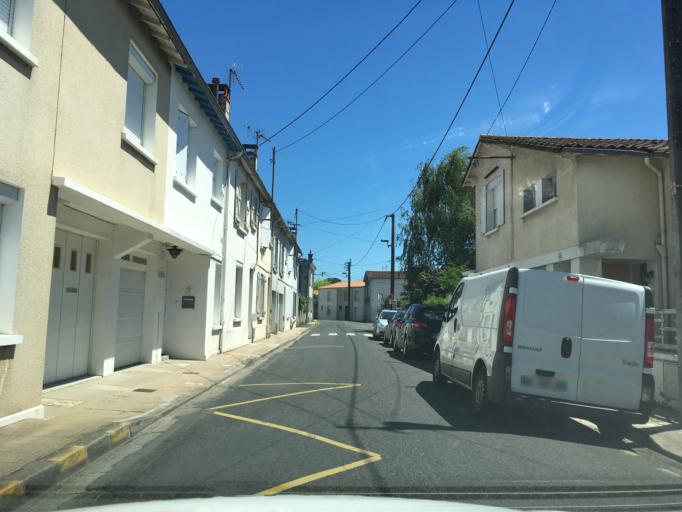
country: FR
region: Poitou-Charentes
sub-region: Departement des Deux-Sevres
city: Niort
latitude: 46.3292
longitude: -0.4484
